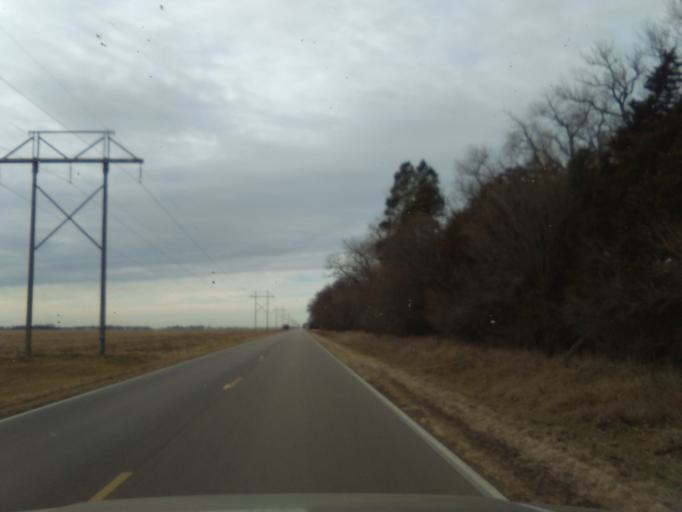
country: US
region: Nebraska
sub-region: Buffalo County
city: Gibbon
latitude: 40.6550
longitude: -98.8126
